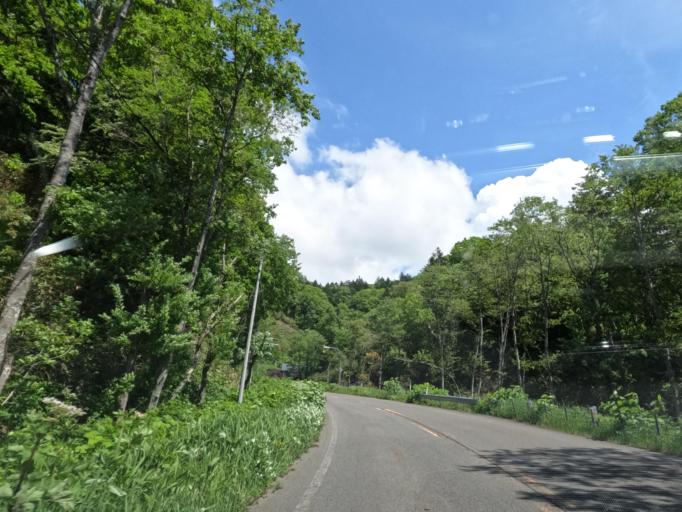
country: JP
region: Hokkaido
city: Takikawa
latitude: 43.5484
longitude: 141.6214
